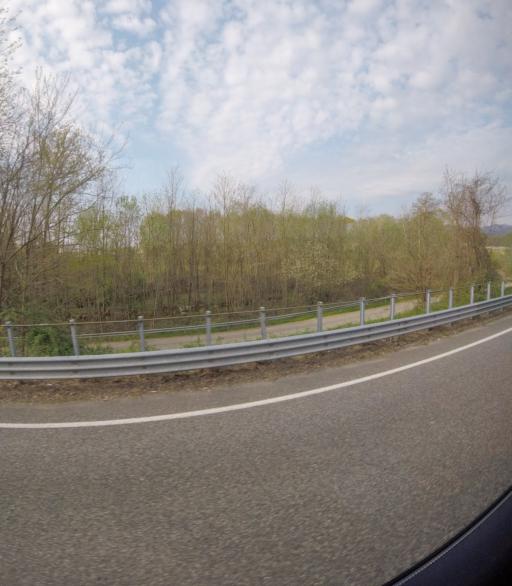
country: IT
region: Piedmont
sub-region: Provincia di Novara
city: Briga Novarese
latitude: 45.7218
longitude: 8.4699
